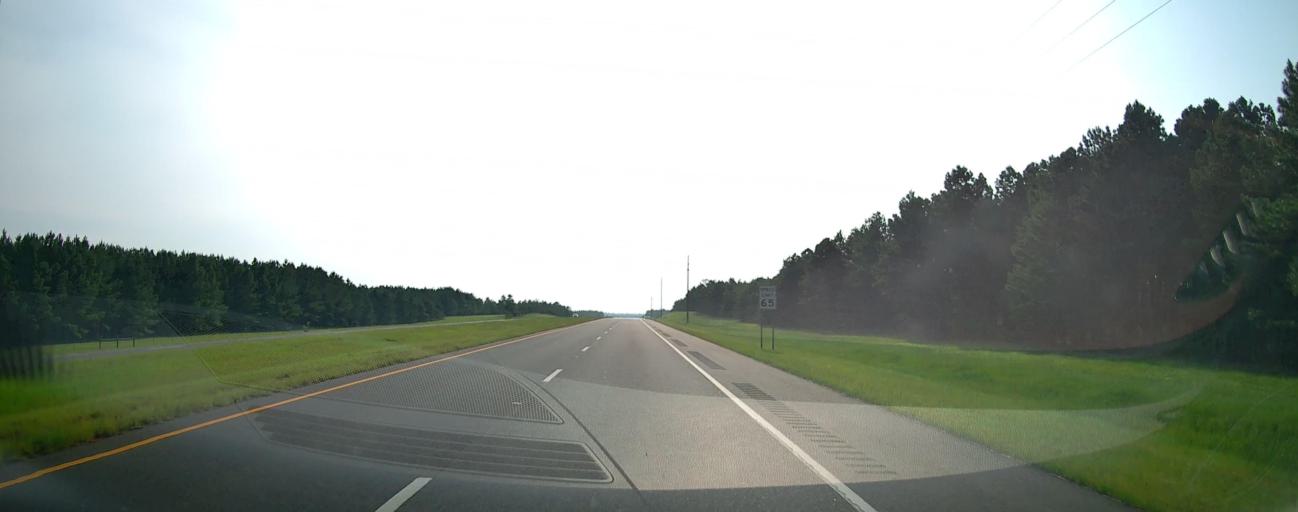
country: US
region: Georgia
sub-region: Talbot County
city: Talbotton
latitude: 32.5946
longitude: -84.4093
